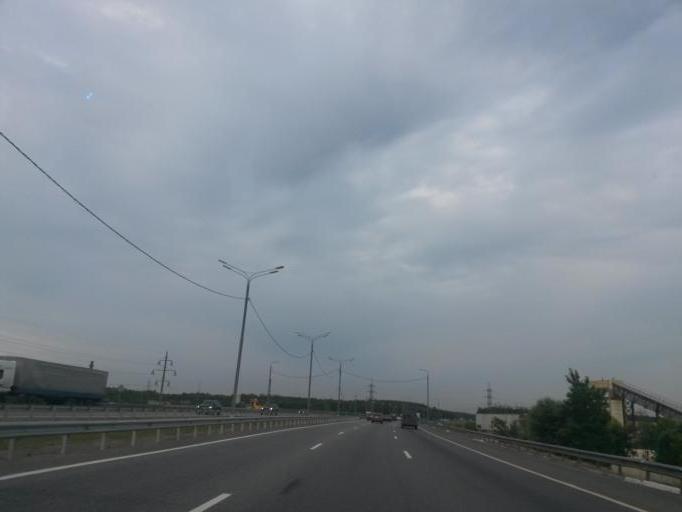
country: RU
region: Moskovskaya
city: Domodedovo
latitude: 55.4607
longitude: 37.7659
